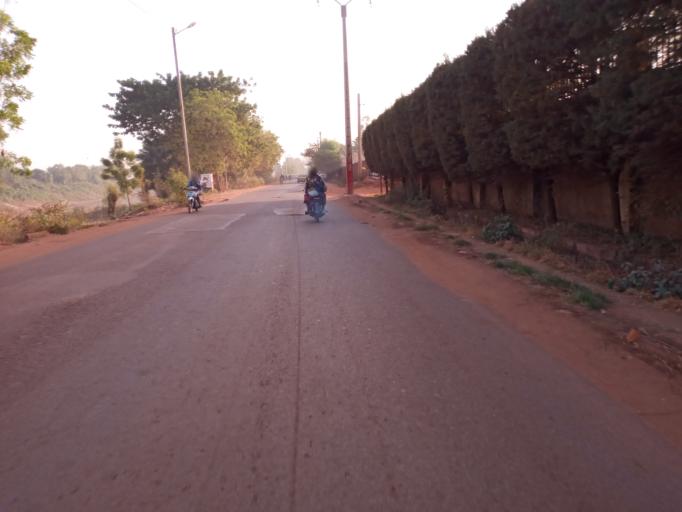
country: ML
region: Bamako
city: Bamako
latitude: 12.6325
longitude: -7.9408
